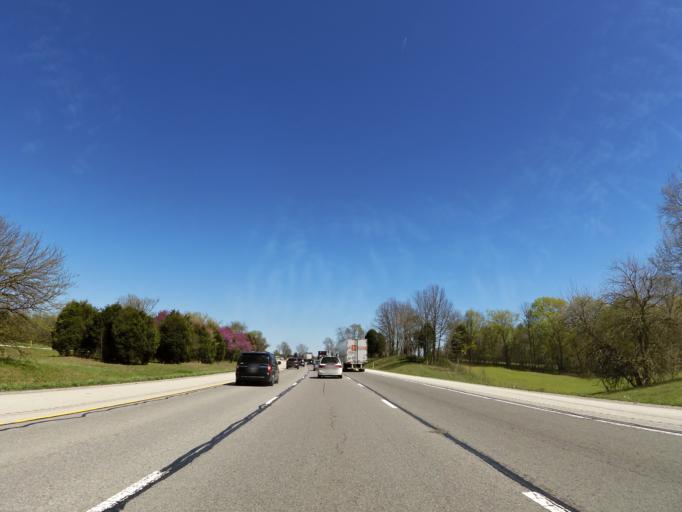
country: US
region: Kentucky
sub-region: Edmonson County
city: Brownsville
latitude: 37.0197
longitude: -86.2548
